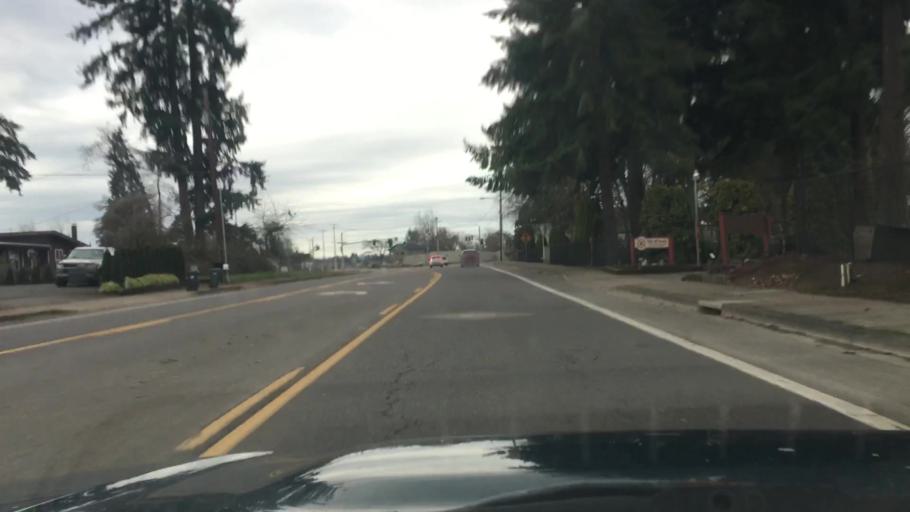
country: US
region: Oregon
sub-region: Lane County
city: Coburg
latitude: 44.1066
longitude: -123.0555
